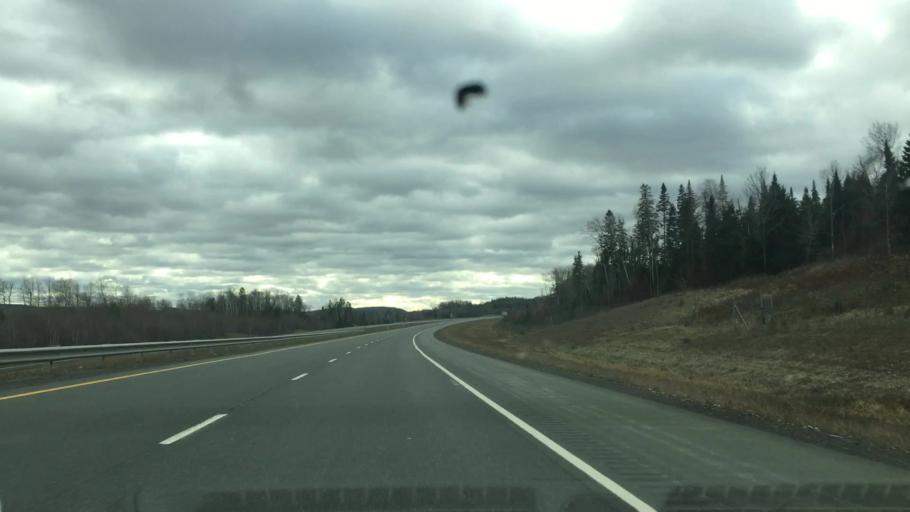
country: US
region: Maine
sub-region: Aroostook County
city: Fort Fairfield
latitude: 46.6767
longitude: -67.7302
